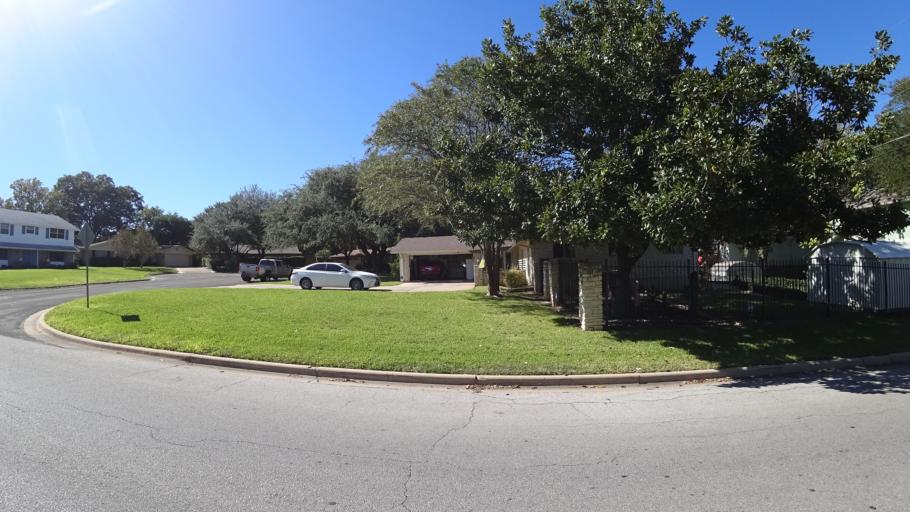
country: US
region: Texas
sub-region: Travis County
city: West Lake Hills
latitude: 30.3253
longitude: -97.7506
